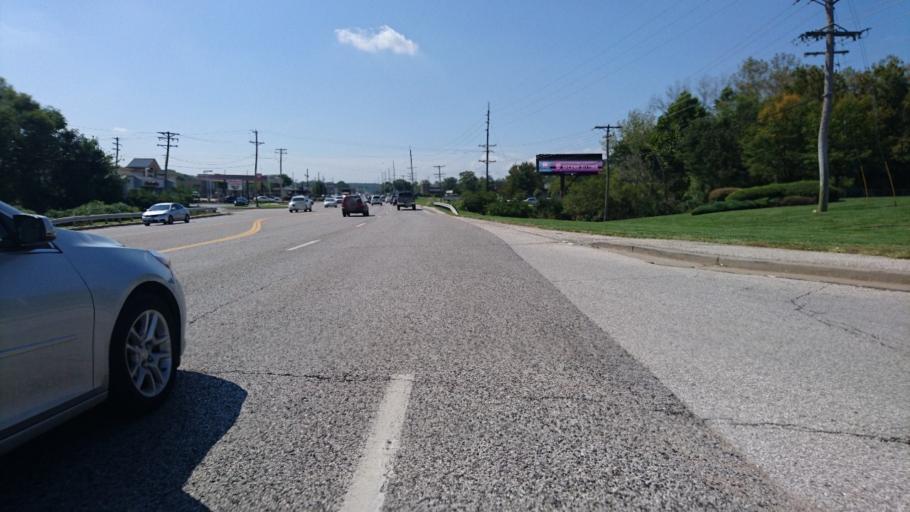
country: US
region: Missouri
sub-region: Saint Louis County
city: Manchester
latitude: 38.5967
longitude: -90.4869
